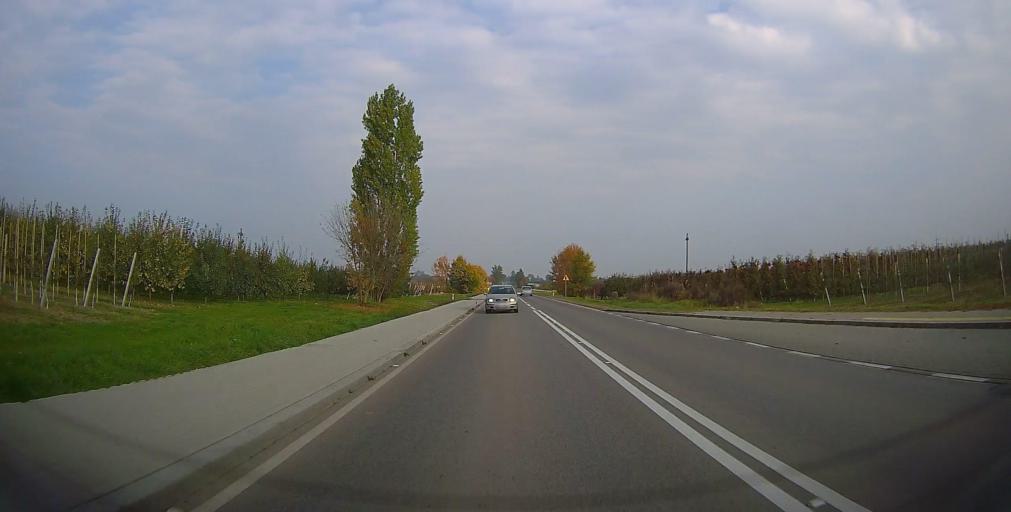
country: PL
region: Masovian Voivodeship
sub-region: Powiat grojecki
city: Bledow
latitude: 51.7642
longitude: 20.7674
